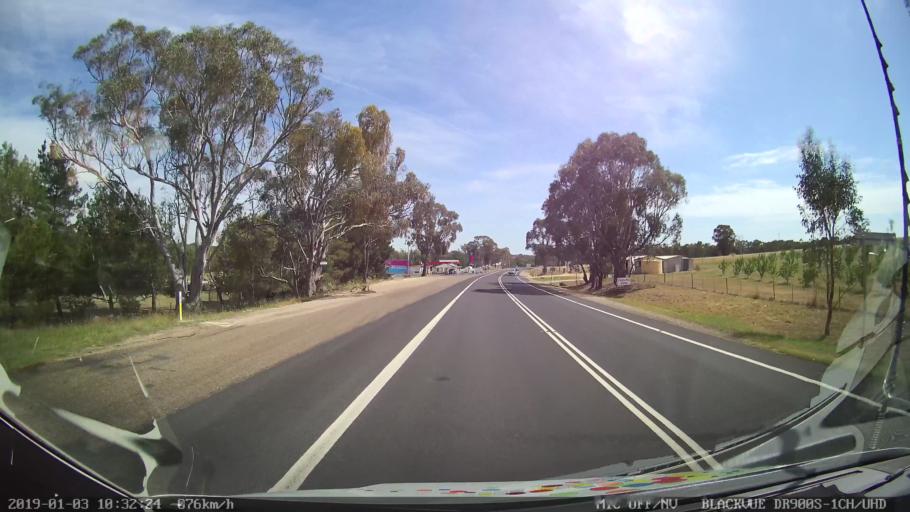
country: AU
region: New South Wales
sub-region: Young
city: Young
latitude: -34.3392
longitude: 148.2829
